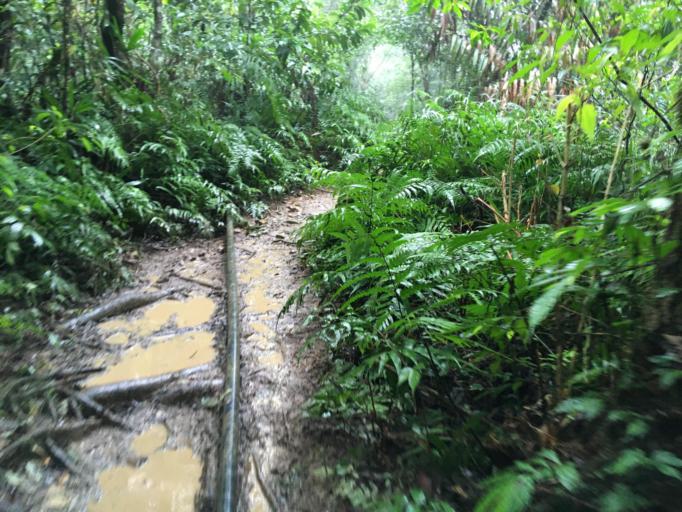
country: TW
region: Taiwan
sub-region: Yilan
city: Yilan
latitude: 24.6780
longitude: 121.5692
